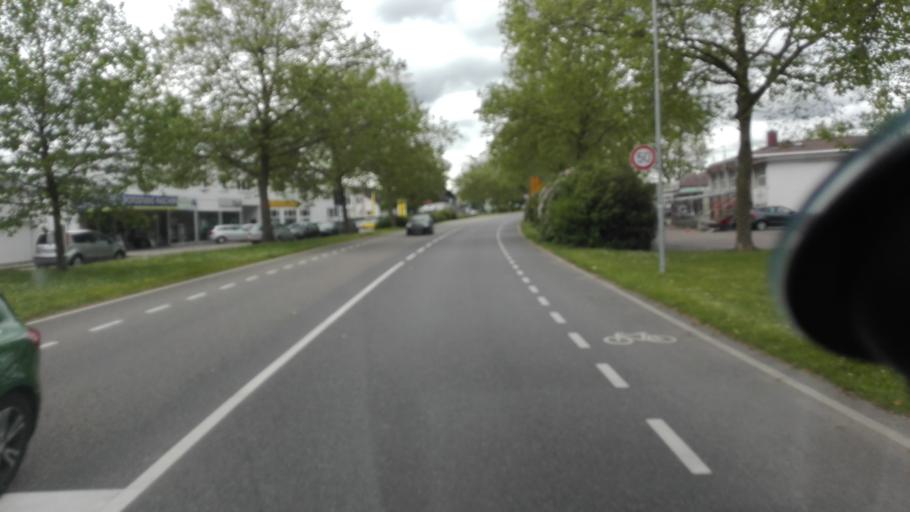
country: DE
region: Baden-Wuerttemberg
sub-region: Karlsruhe Region
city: Kronau
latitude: 49.2169
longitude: 8.6527
